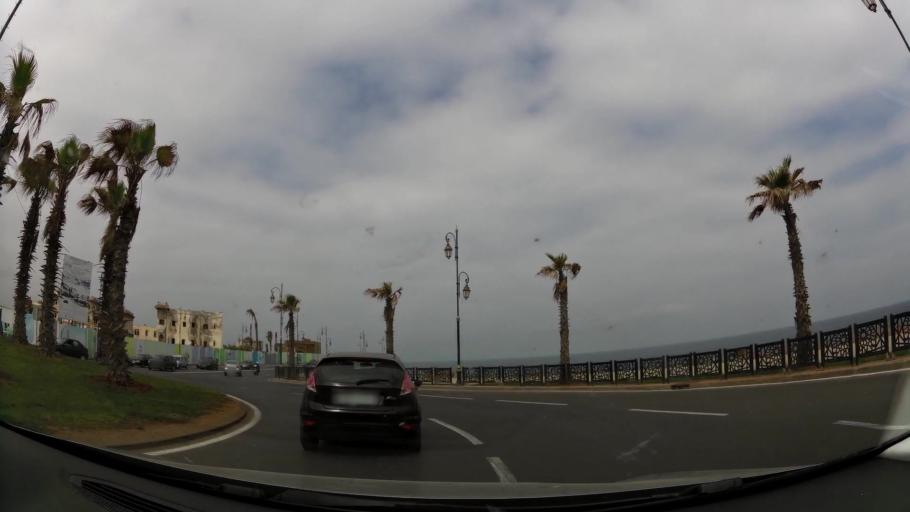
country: MA
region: Rabat-Sale-Zemmour-Zaer
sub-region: Rabat
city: Rabat
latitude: 34.0220
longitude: -6.8533
